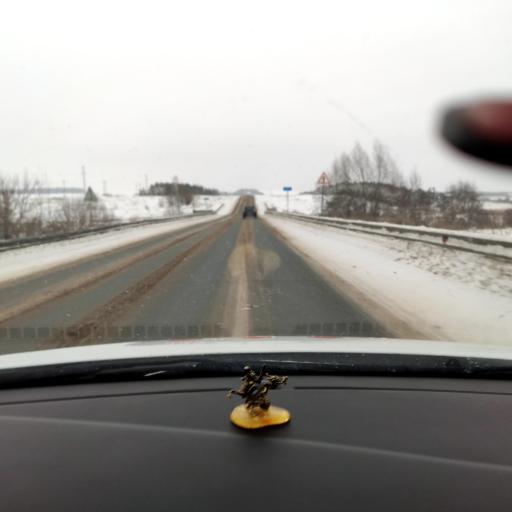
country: RU
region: Tatarstan
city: Vysokaya Gora
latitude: 56.0185
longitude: 49.2680
